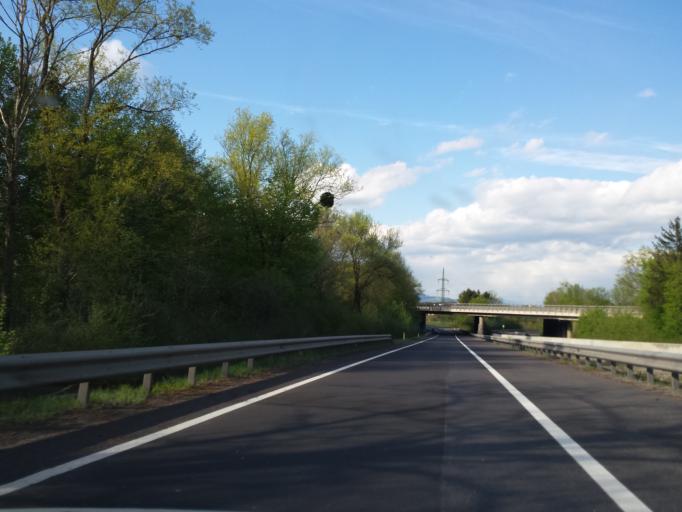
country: AT
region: Styria
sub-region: Politischer Bezirk Graz-Umgebung
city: Seiersberg
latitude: 46.9979
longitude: 15.4080
